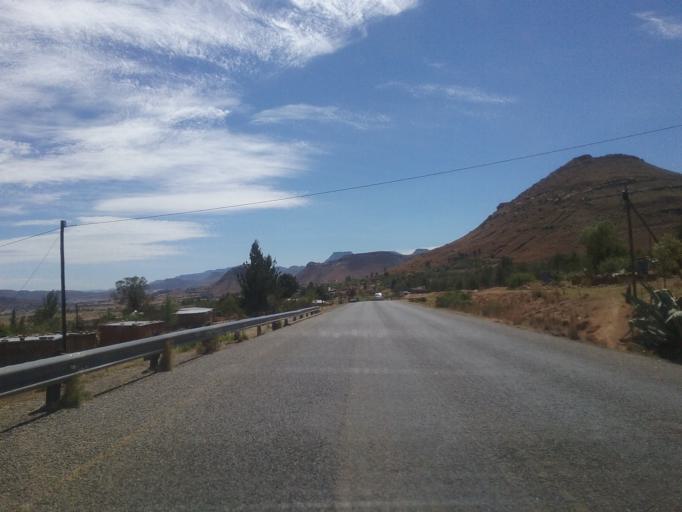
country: LS
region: Mohale's Hoek District
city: Mohale's Hoek
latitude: -30.1875
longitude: 27.4188
